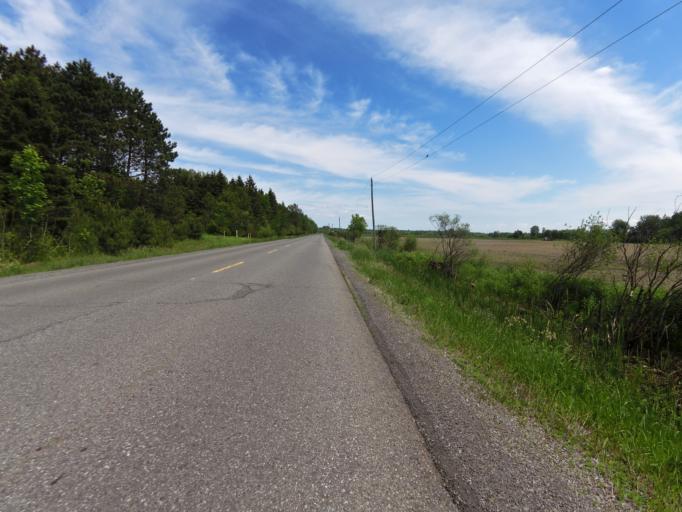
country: CA
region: Ontario
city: Ottawa
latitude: 45.3603
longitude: -75.5814
